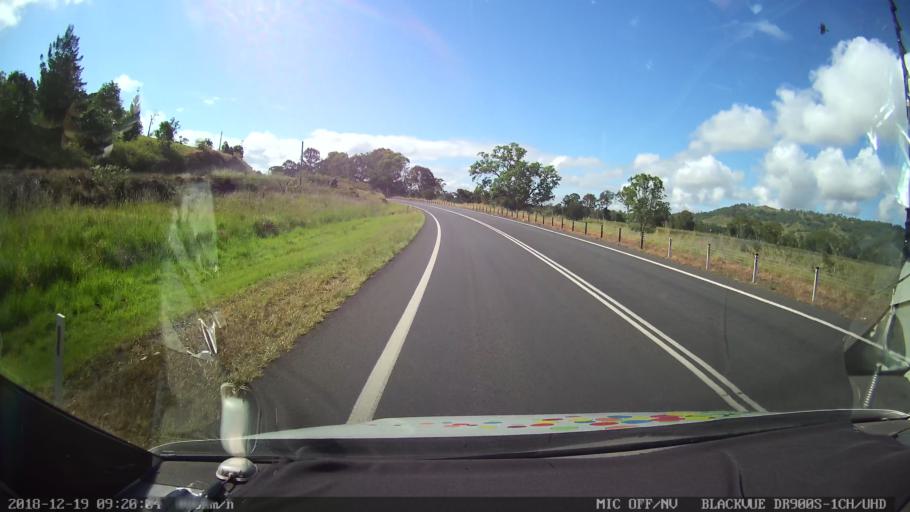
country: AU
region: New South Wales
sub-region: Kyogle
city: Kyogle
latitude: -28.5681
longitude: 152.9778
